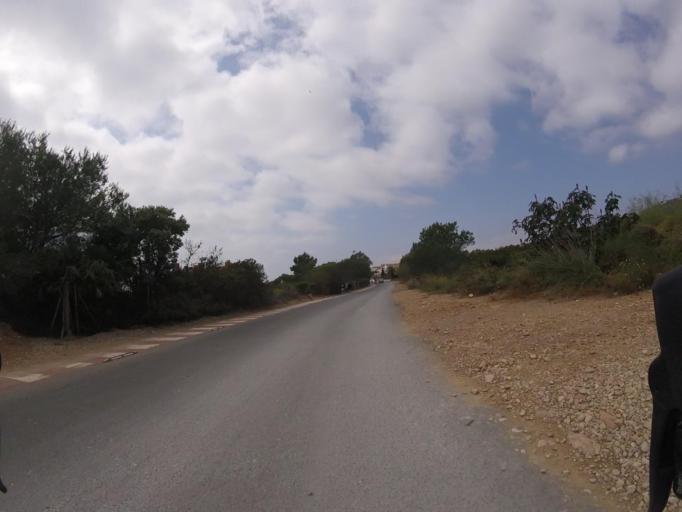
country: ES
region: Valencia
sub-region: Provincia de Castello
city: Alcoceber
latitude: 40.2582
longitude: 0.2950
